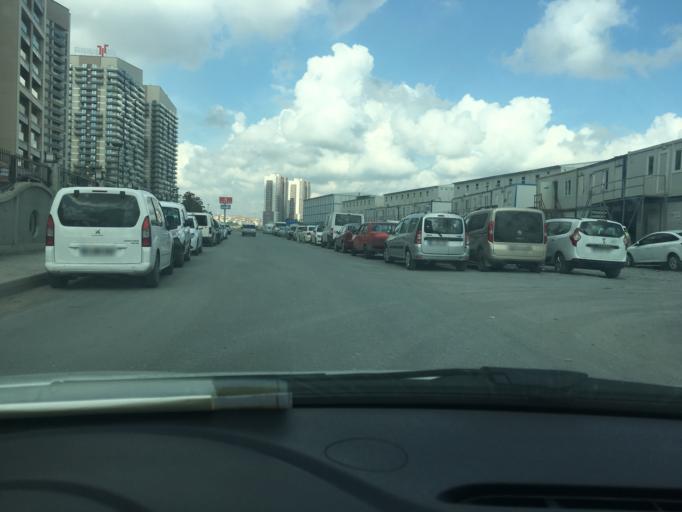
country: TR
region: Istanbul
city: Sisli
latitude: 41.0923
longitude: 28.9488
